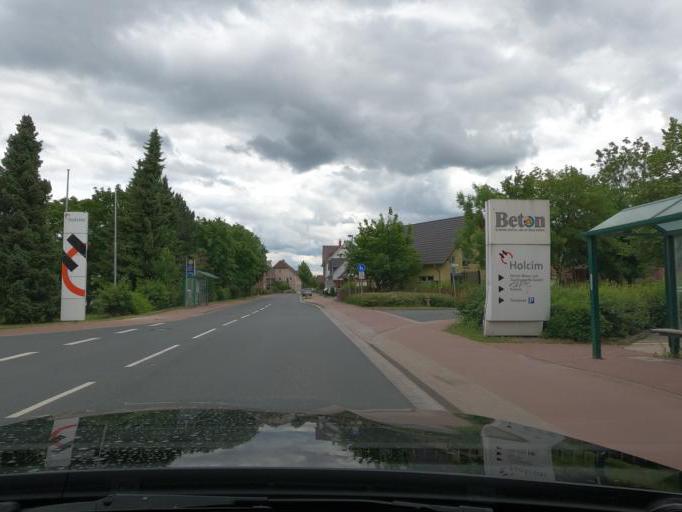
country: DE
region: Lower Saxony
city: Sehnde
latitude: 52.3514
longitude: 9.8883
